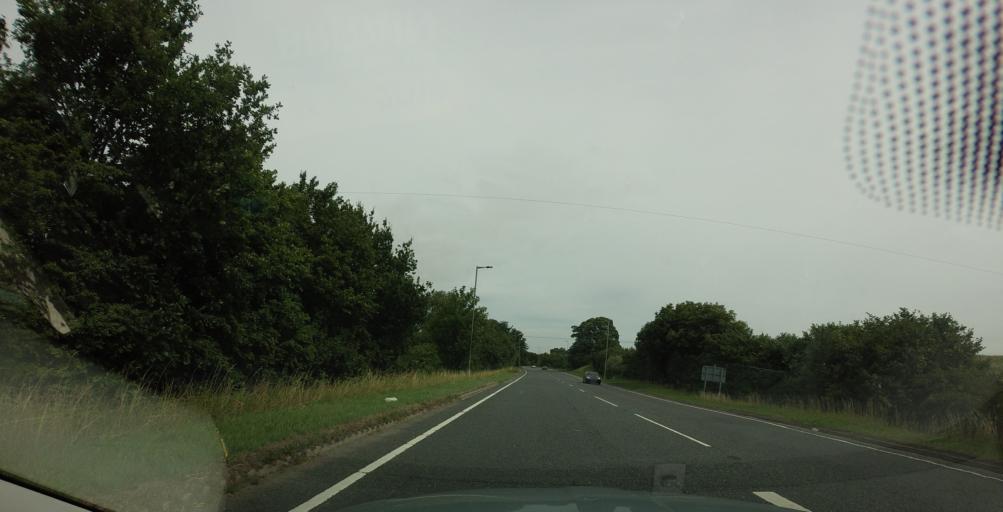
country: GB
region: England
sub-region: North Yorkshire
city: Ripon
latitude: 54.1260
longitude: -1.5152
